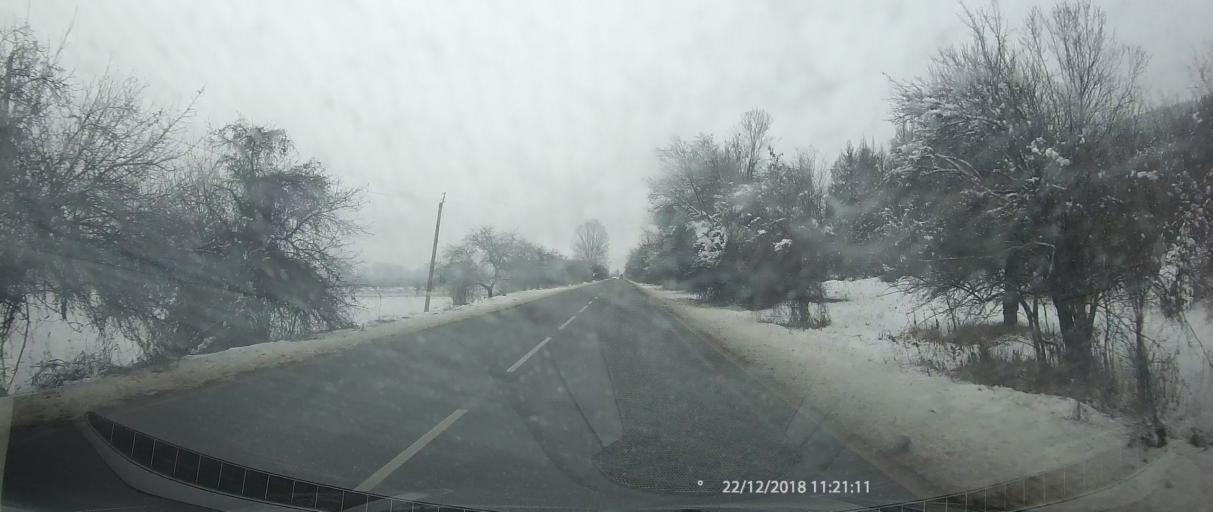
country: BG
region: Kyustendil
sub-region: Obshtina Kyustendil
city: Kyustendil
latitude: 42.2592
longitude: 22.8357
